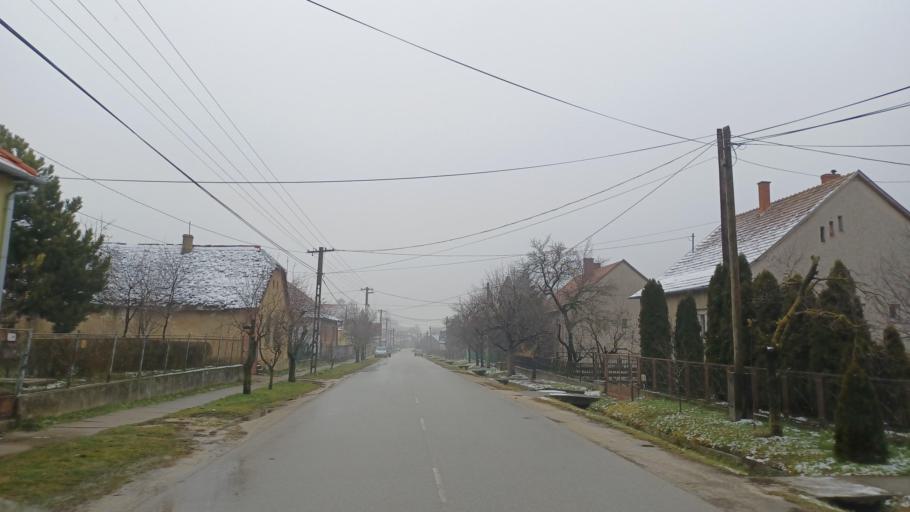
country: HU
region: Tolna
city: Gyonk
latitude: 46.5615
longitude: 18.4777
